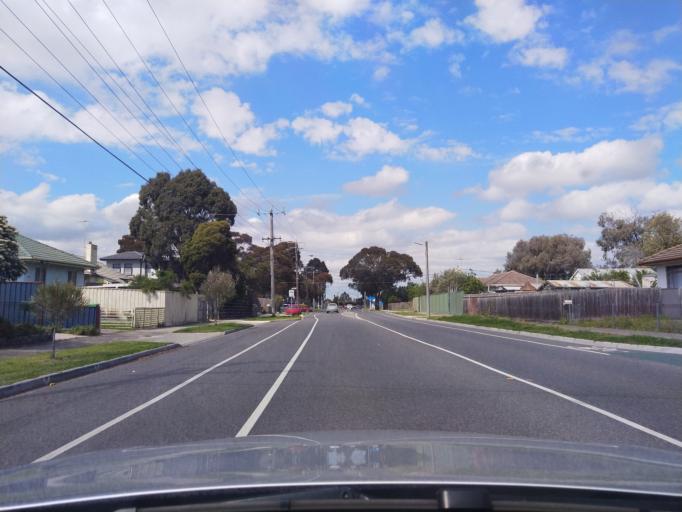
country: AU
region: Victoria
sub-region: Banyule
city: Bellfield
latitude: -37.7470
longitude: 145.0419
